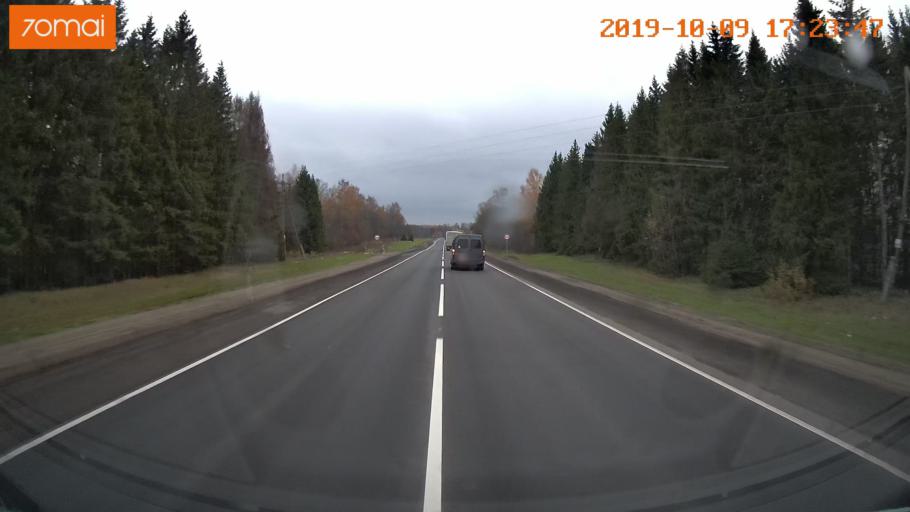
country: RU
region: Ivanovo
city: Furmanov
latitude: 57.1917
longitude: 41.1138
